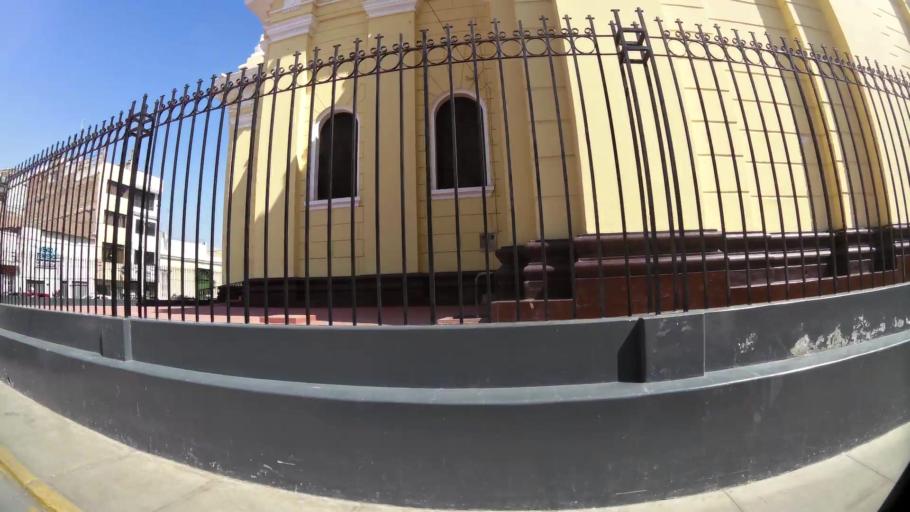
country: PE
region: Lambayeque
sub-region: Provincia de Chiclayo
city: Chiclayo
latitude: -6.7715
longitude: -79.8374
